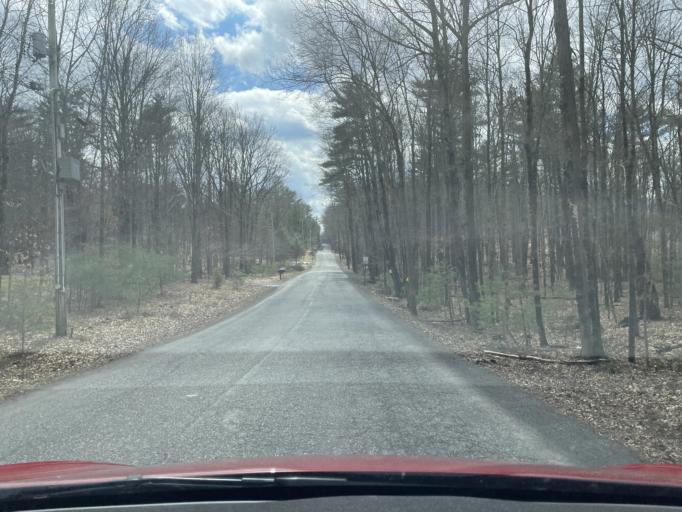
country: US
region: New York
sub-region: Ulster County
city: Zena
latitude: 42.0705
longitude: -74.0334
